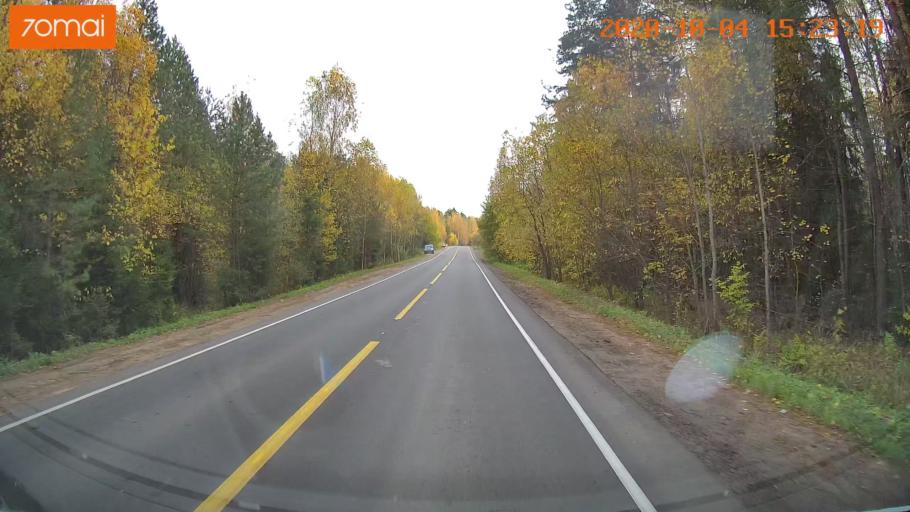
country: RU
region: Ivanovo
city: Bogorodskoye
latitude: 57.0747
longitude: 40.9479
